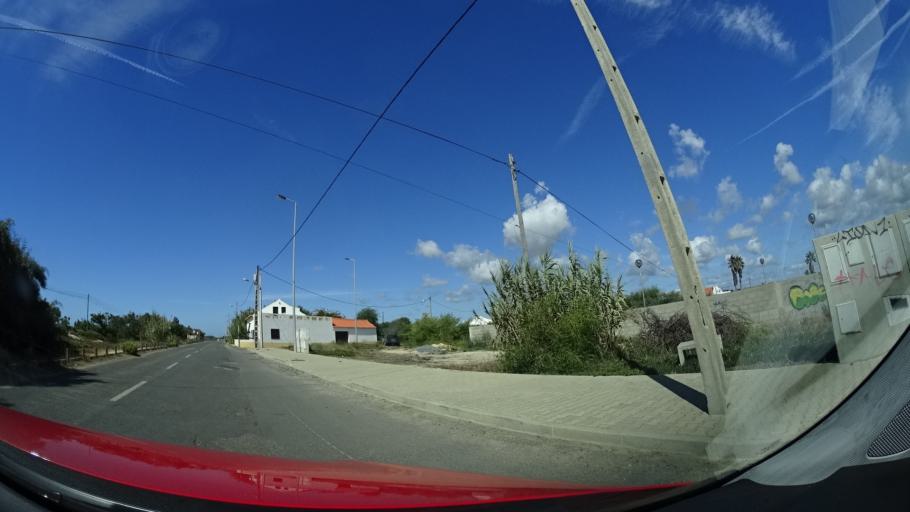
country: PT
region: Beja
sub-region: Odemira
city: Sao Teotonio
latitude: 37.5278
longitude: -8.7842
